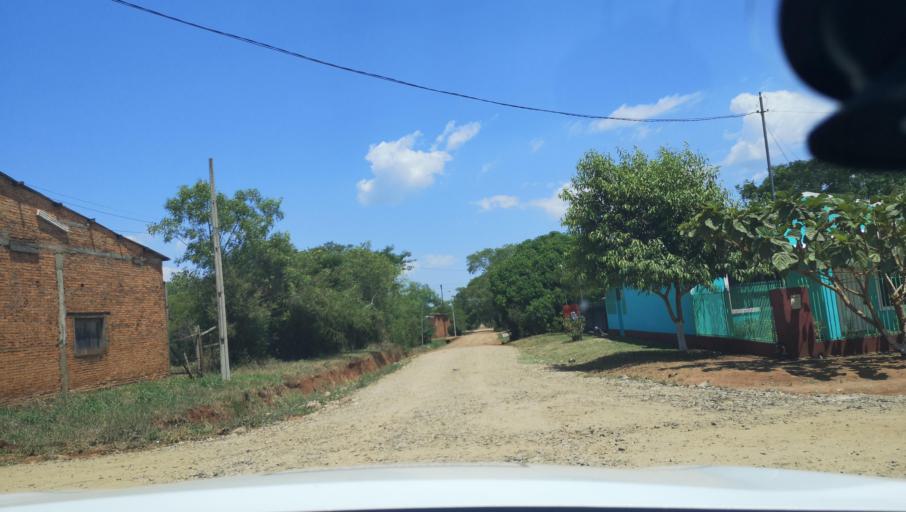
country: PY
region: Itapua
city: Carmen del Parana
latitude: -27.1654
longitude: -56.2373
